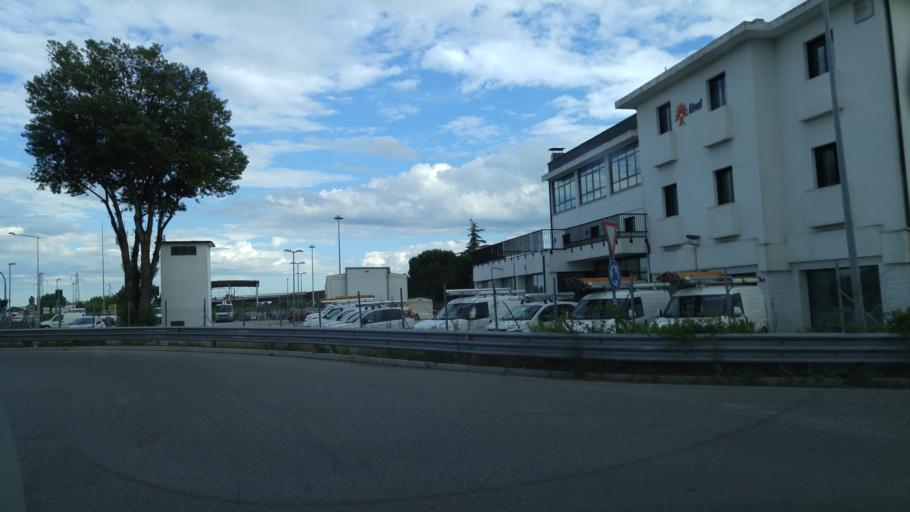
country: IT
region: Emilia-Romagna
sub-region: Provincia di Rimini
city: Rimini
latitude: 44.0461
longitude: 12.5526
